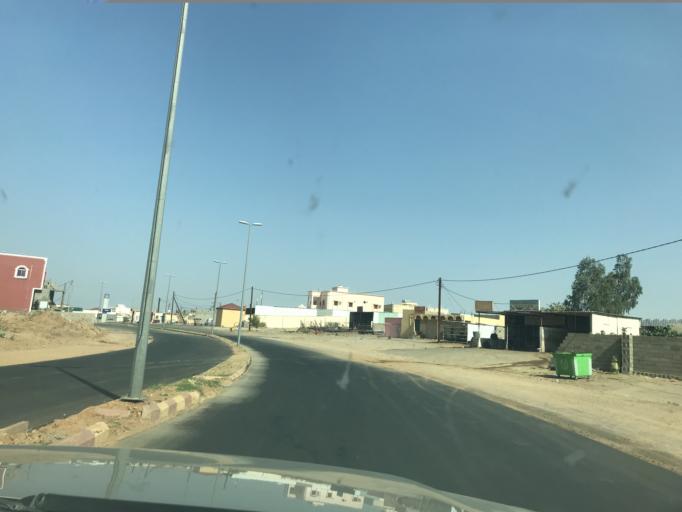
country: SA
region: Mintaqat al Bahah
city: Al Bahah
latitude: 20.4401
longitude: 41.9268
